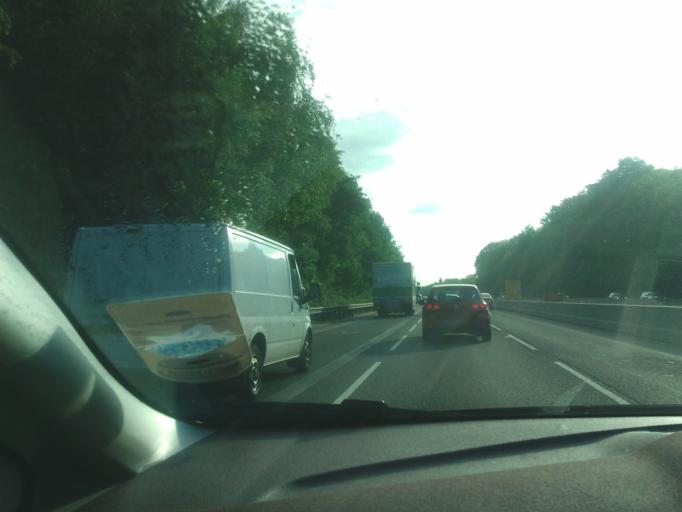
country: GB
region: England
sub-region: Surrey
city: Windlesham
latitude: 51.3622
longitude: -0.6449
